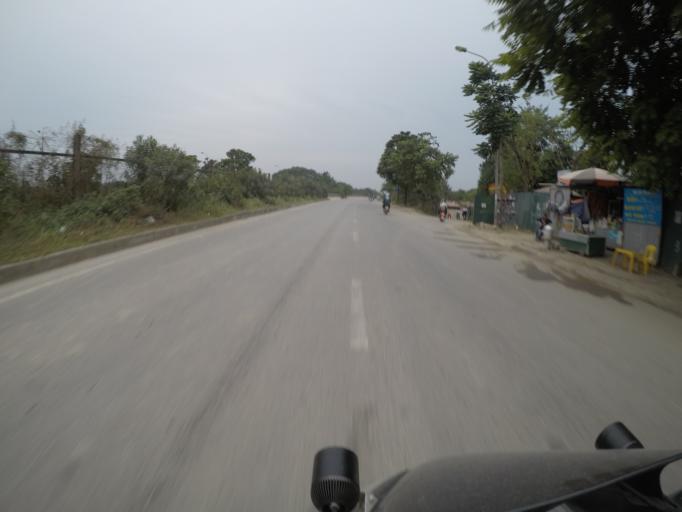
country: VN
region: Ha Noi
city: Cau Dien
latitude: 21.0068
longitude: 105.7641
